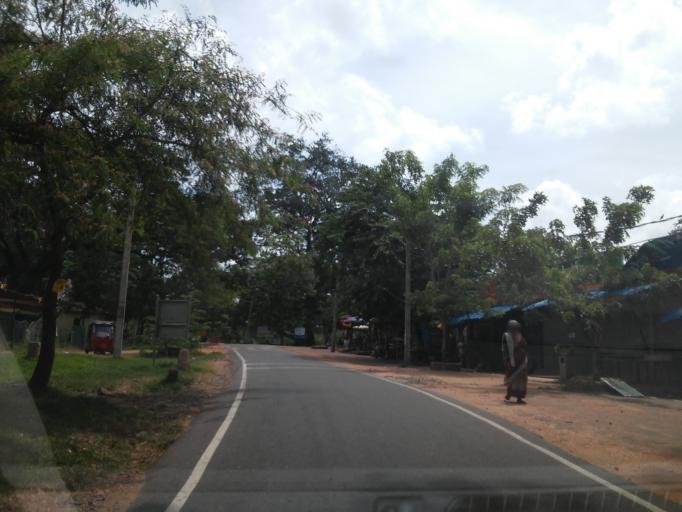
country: LK
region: North Central
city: Anuradhapura
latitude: 8.3514
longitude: 80.3987
